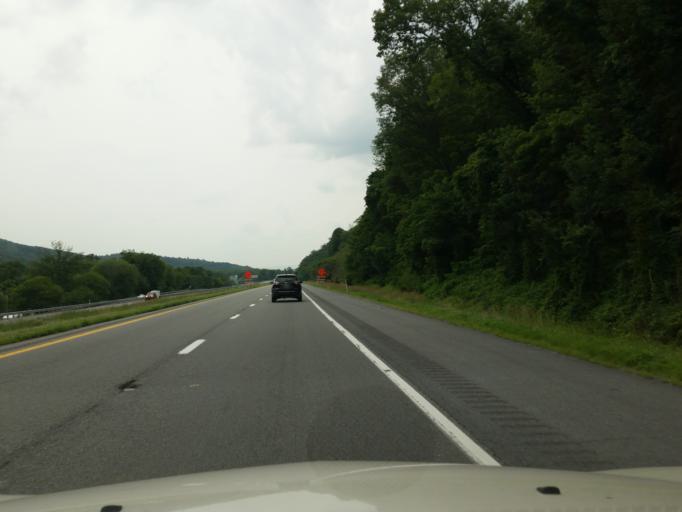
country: US
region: Pennsylvania
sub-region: Perry County
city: Newport
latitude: 40.5656
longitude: -77.1781
